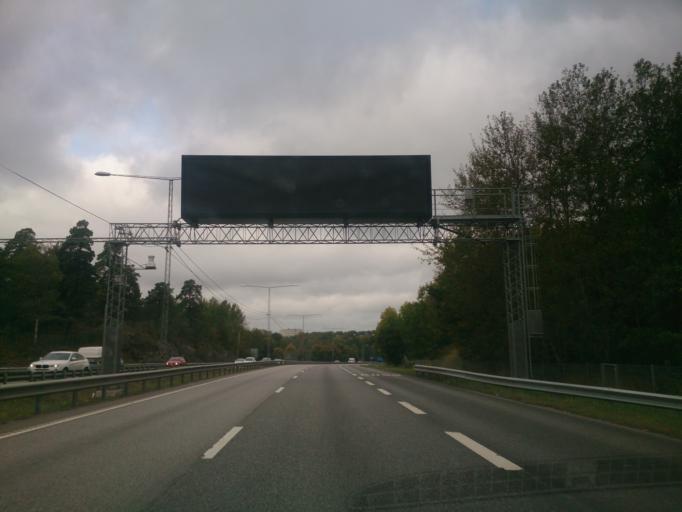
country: SE
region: Stockholm
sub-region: Stockholms Kommun
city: Arsta
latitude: 59.2468
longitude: 18.1020
